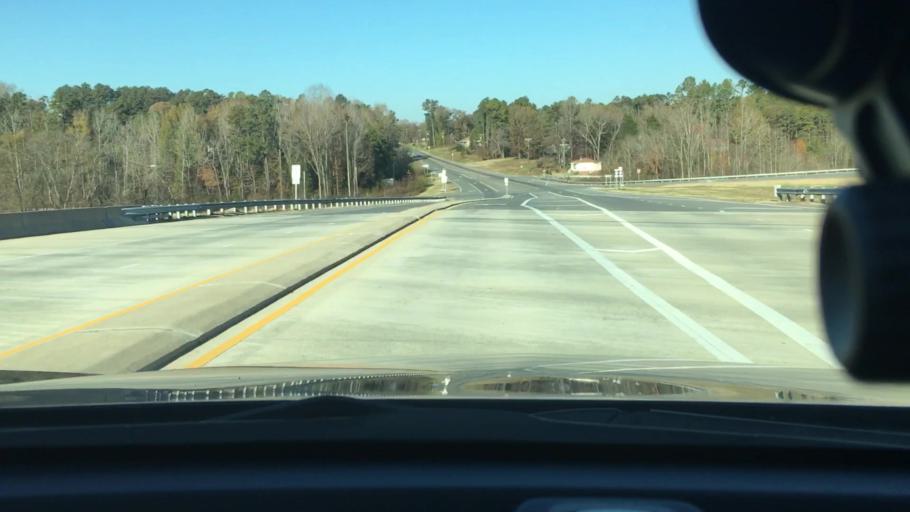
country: US
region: North Carolina
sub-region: Cabarrus County
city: Mount Pleasant
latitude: 35.4069
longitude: -80.4521
